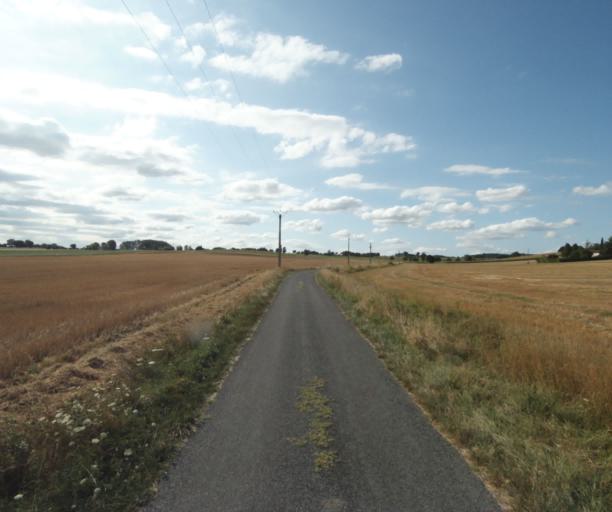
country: FR
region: Midi-Pyrenees
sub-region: Departement du Tarn
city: Puylaurens
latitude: 43.5264
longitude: 2.0007
